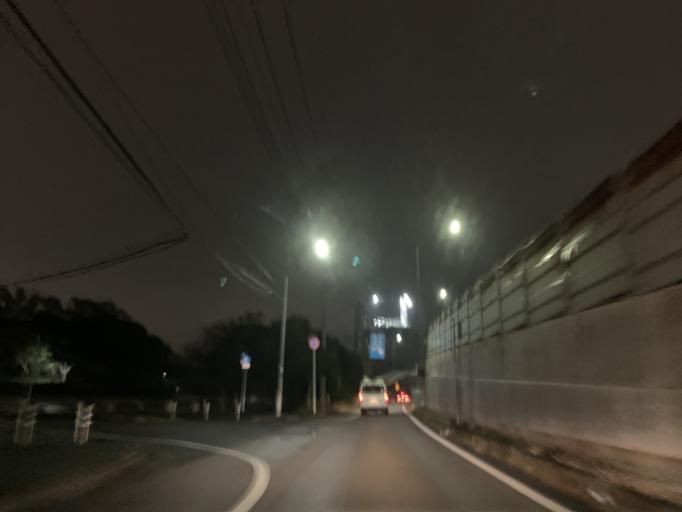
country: JP
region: Chiba
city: Funabashi
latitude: 35.6571
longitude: 140.0328
